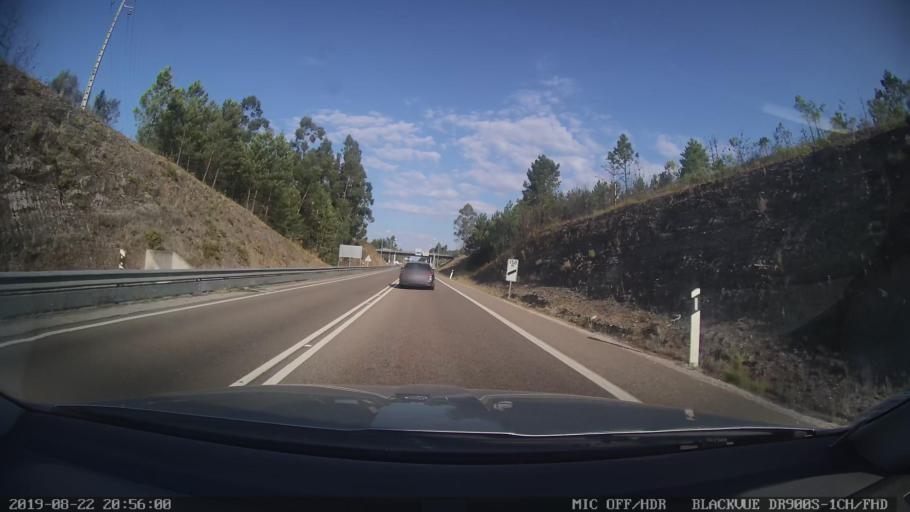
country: PT
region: Castelo Branco
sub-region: Serta
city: Serta
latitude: 39.7860
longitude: -8.0429
